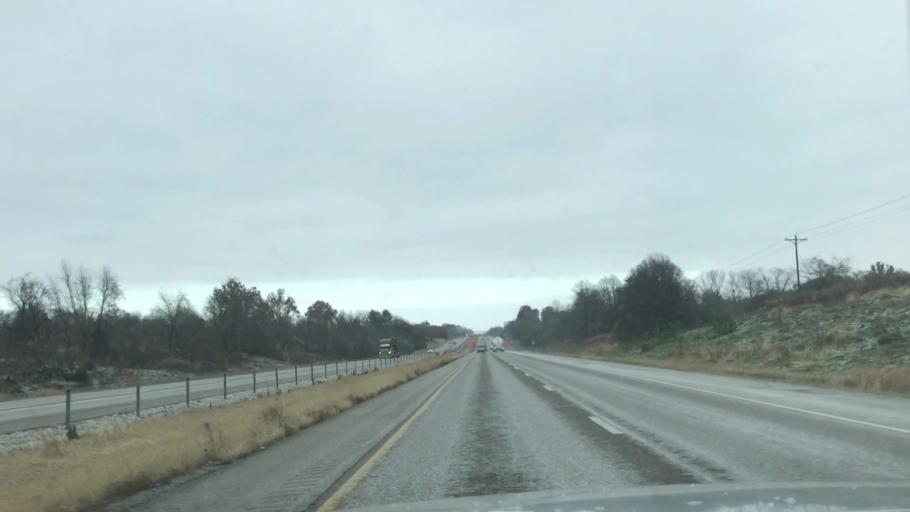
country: US
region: Illinois
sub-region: Madison County
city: Troy
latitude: 38.7623
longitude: -89.9043
